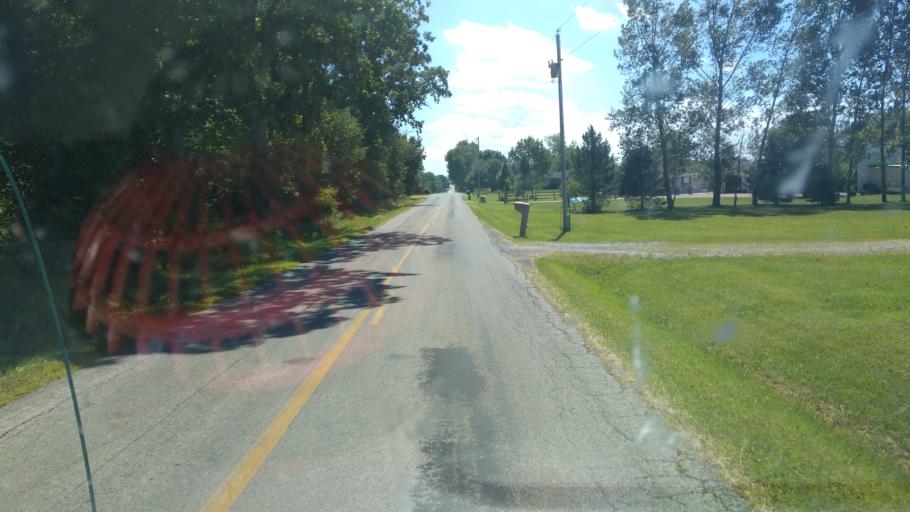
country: US
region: Ohio
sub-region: Marion County
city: Marion
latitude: 40.6600
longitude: -83.1733
